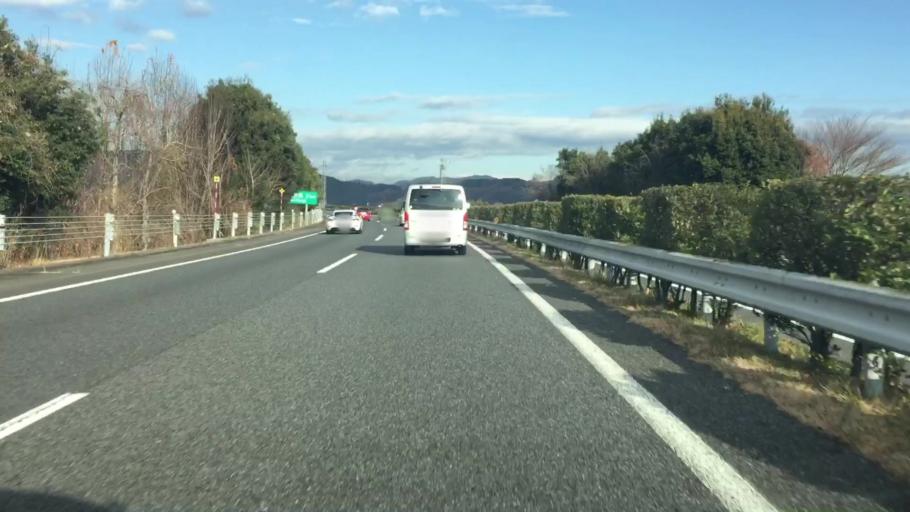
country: JP
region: Gunma
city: Annaka
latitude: 36.3006
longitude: 138.7963
